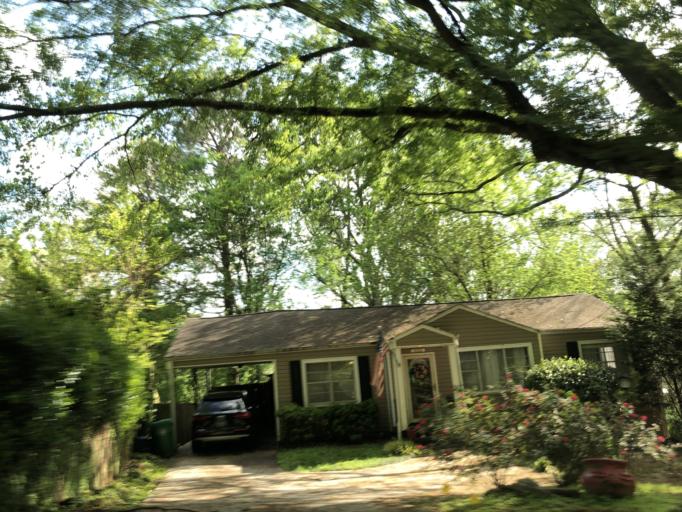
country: US
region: Georgia
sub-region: DeKalb County
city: North Druid Hills
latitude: 33.8085
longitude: -84.3404
